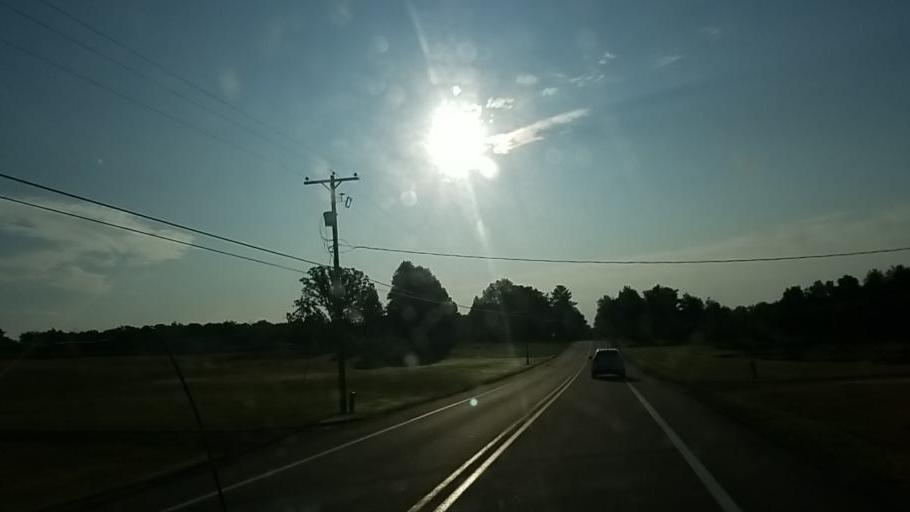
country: US
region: Michigan
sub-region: Montcalm County
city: Stanton
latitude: 43.2500
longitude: -85.1166
